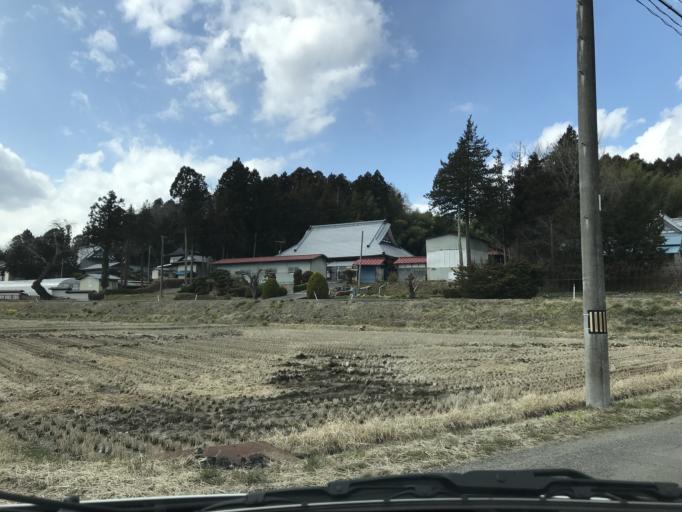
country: JP
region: Miyagi
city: Wakuya
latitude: 38.6908
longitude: 141.1448
